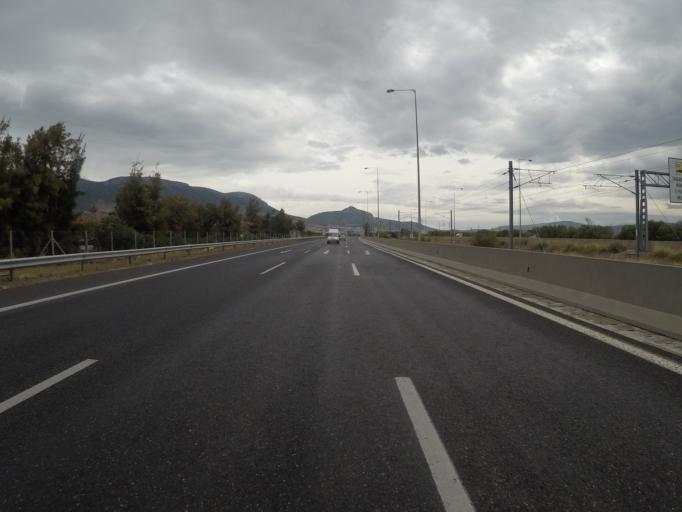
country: GR
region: Attica
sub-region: Nomarchia Dytikis Attikis
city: Aspropyrgos
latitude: 38.0946
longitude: 23.5688
